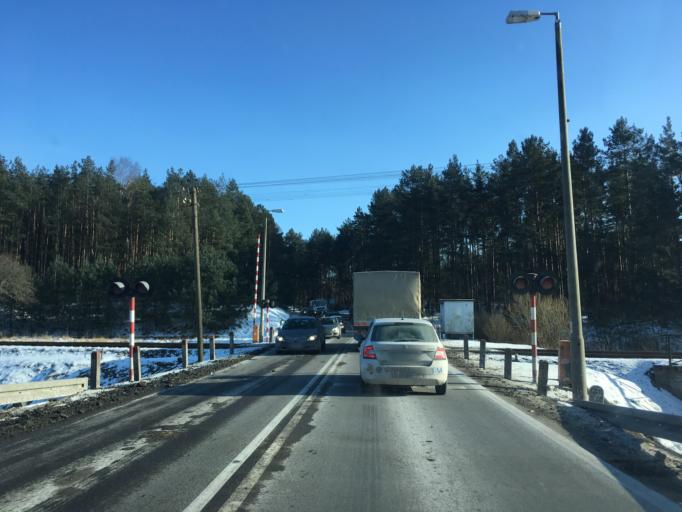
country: PL
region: Pomeranian Voivodeship
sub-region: Powiat koscierski
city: Koscierzyna
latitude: 54.1182
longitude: 17.8893
